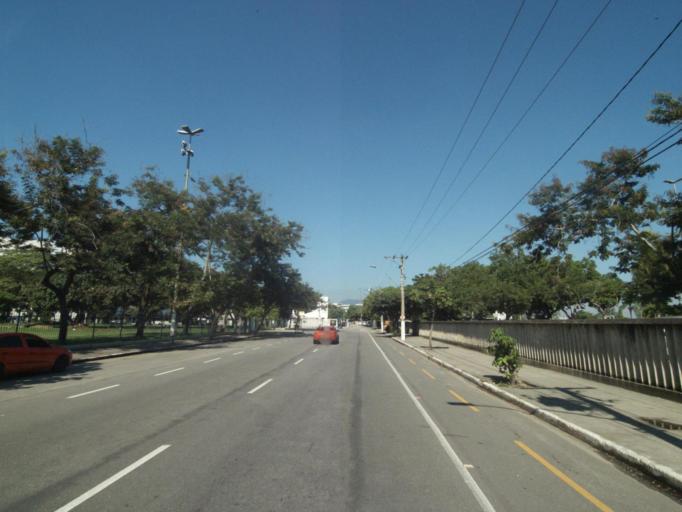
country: BR
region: Rio de Janeiro
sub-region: Niteroi
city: Niteroi
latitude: -22.8968
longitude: -43.1291
